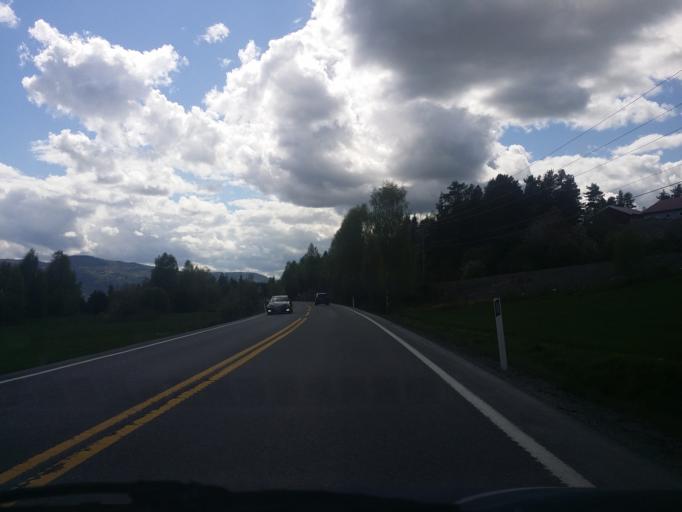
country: NO
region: Buskerud
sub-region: Modum
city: Vikersund
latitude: 59.9635
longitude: 9.9805
